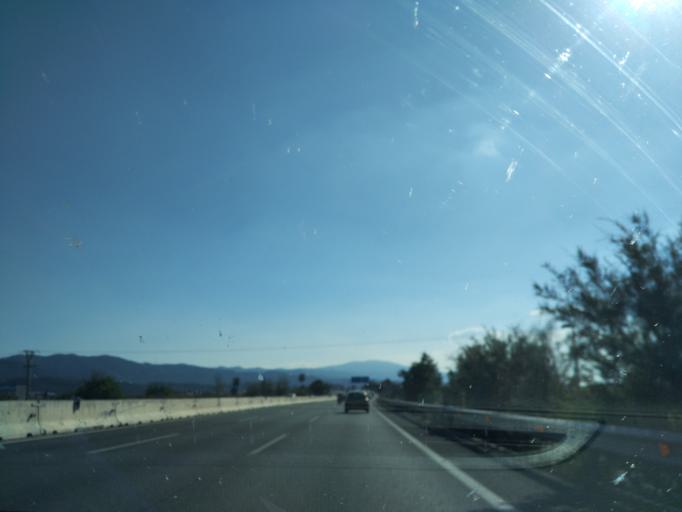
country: ES
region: Murcia
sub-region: Murcia
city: Murcia
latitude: 37.9528
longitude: -1.1410
